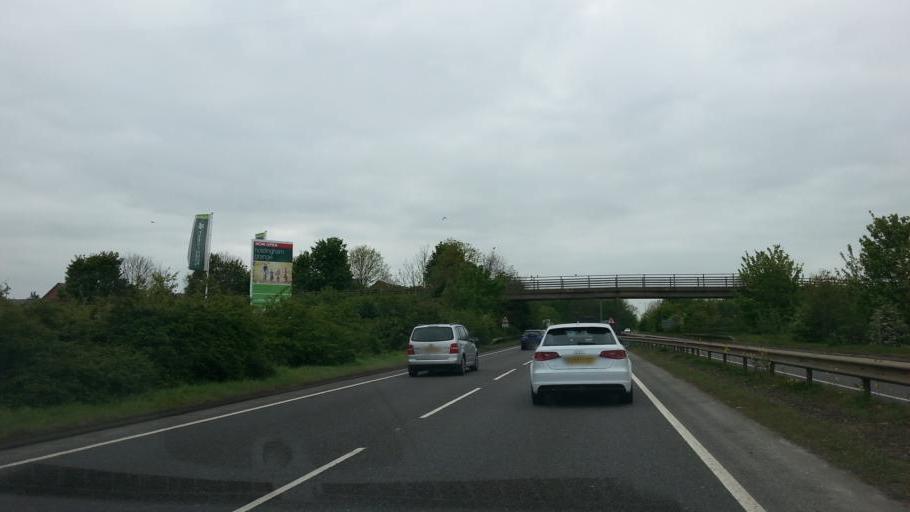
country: GB
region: England
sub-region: Lincolnshire
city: Leasingham
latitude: 53.0132
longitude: -0.4195
